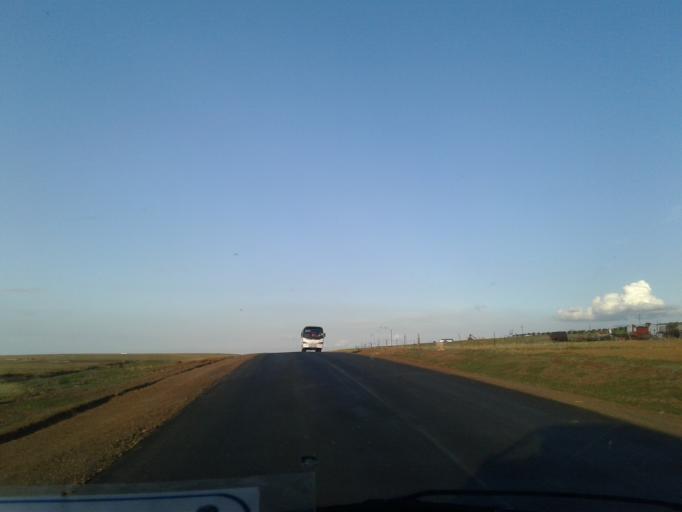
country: LS
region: Maseru
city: Maseru
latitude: -29.3110
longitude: 27.5984
